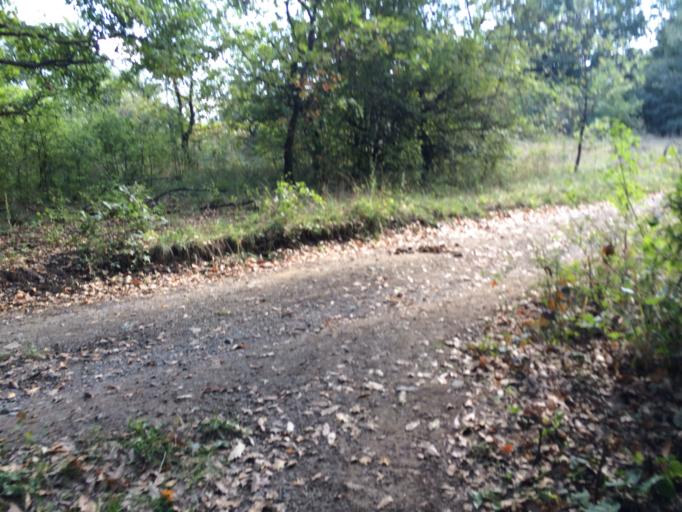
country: HU
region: Pest
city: Nagymaros
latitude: 47.8259
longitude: 18.9455
